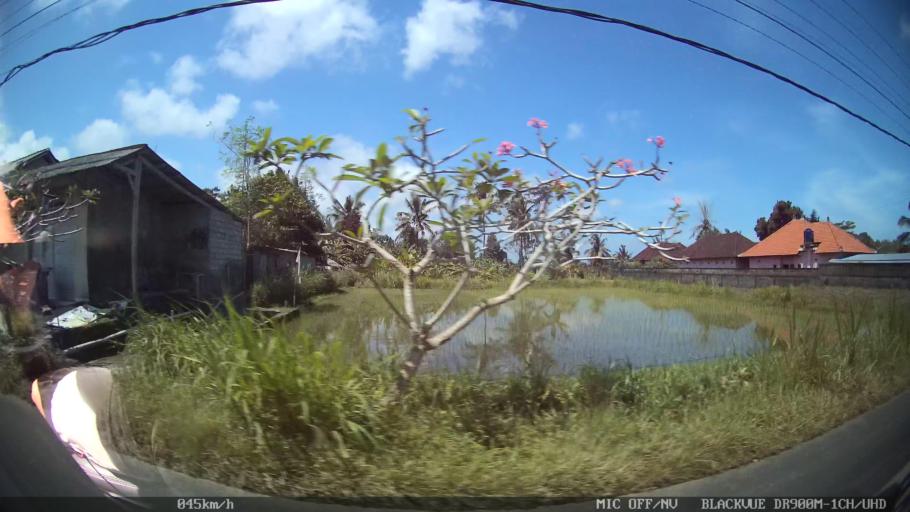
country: ID
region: Bali
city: Banjar Kelodan
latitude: -8.5300
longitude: 115.3357
